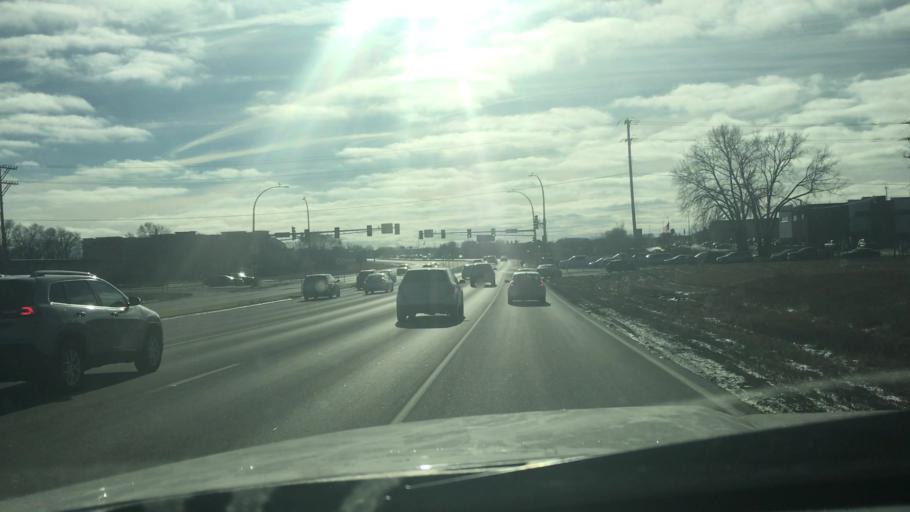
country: US
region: Minnesota
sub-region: Stearns County
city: Waite Park
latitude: 45.5597
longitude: -94.2061
